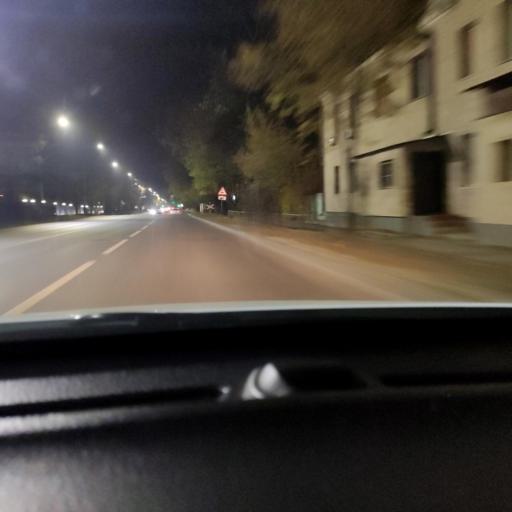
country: RU
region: Voronezj
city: Somovo
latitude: 51.7122
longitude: 39.2757
